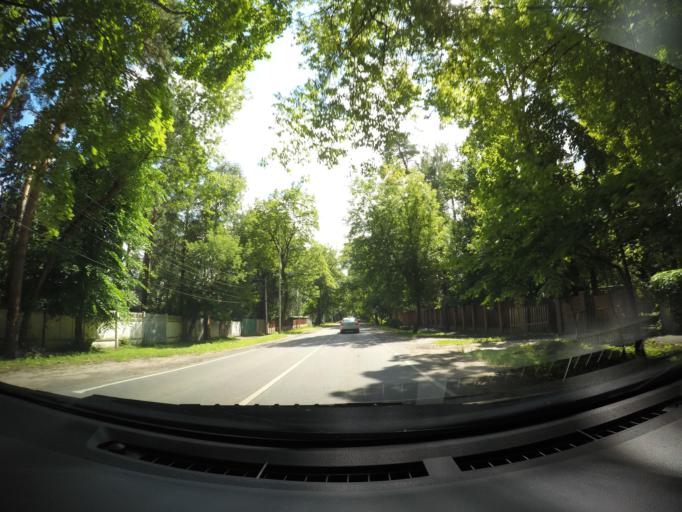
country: RU
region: Moskovskaya
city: Kraskovo
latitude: 55.6532
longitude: 37.9938
